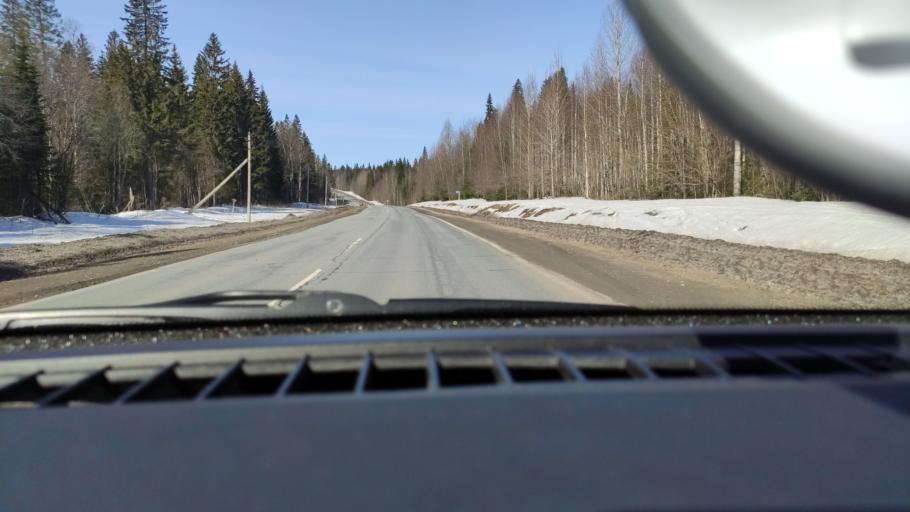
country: RU
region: Perm
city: Perm
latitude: 58.2002
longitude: 56.2060
